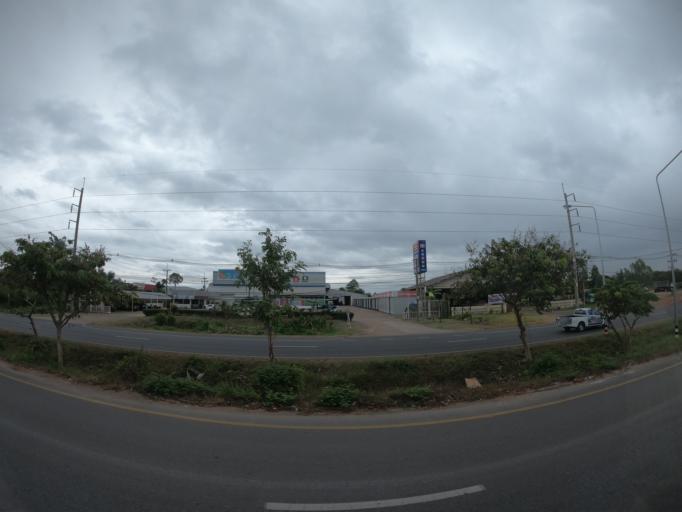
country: TH
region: Roi Et
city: Roi Et
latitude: 16.0533
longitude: 103.6202
